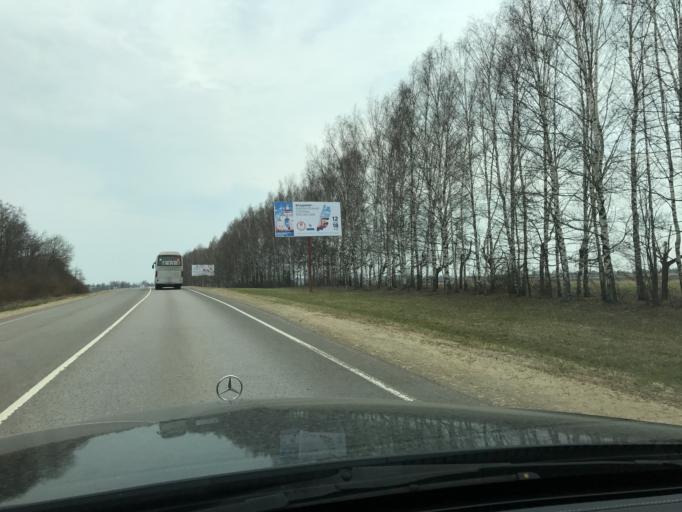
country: RU
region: Vladimir
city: Suzdal'
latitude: 56.3954
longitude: 40.4505
